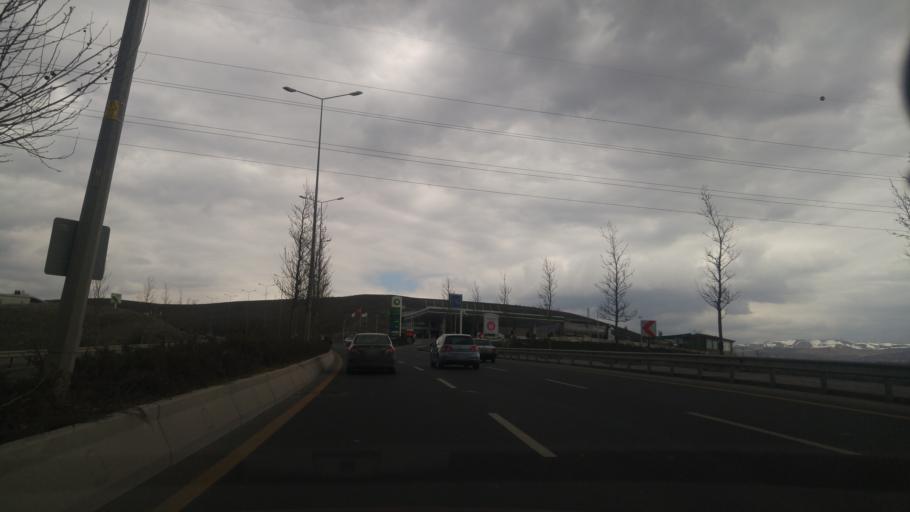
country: TR
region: Ankara
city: Mamak
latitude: 39.8850
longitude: 32.9173
